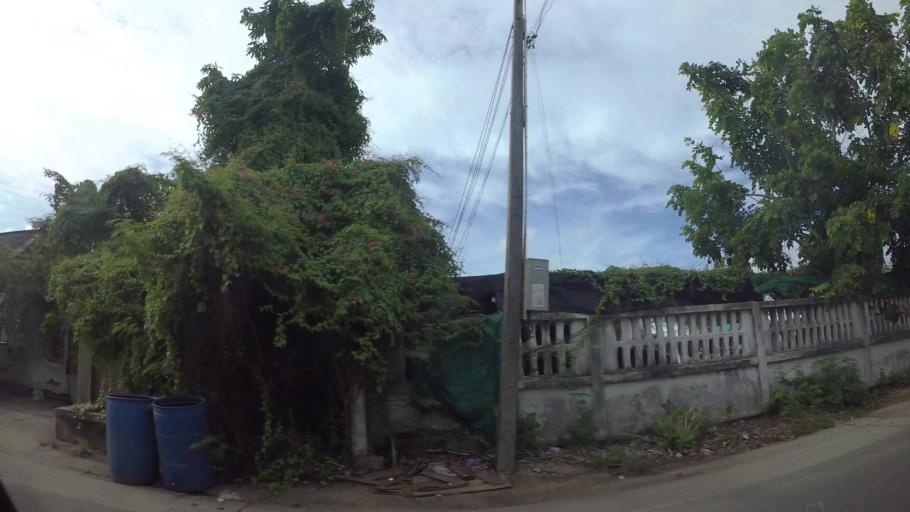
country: TH
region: Rayong
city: Rayong
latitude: 12.6629
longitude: 101.2636
